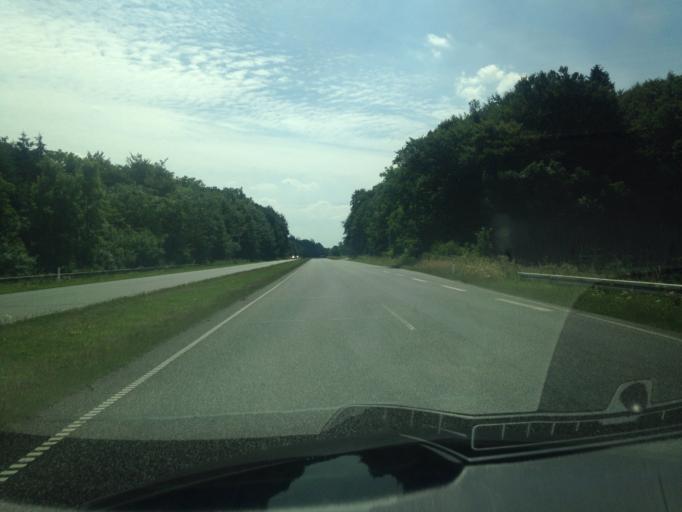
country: DK
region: South Denmark
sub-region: Kolding Kommune
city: Kolding
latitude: 55.5233
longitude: 9.4980
